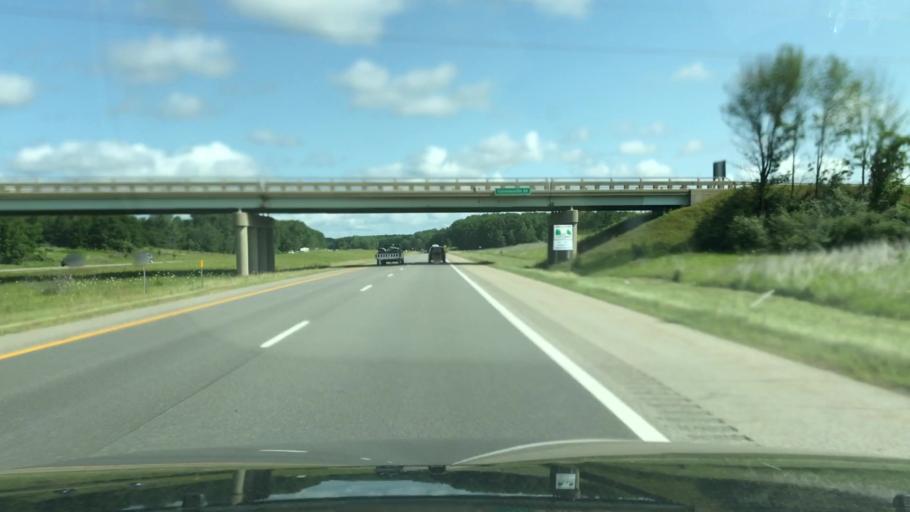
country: US
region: Michigan
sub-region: Montcalm County
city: Howard City
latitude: 43.3371
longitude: -85.5117
